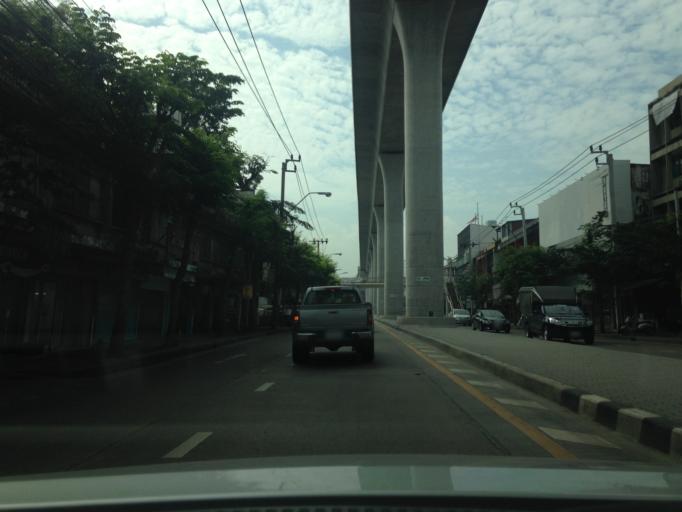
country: TH
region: Bangkok
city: Bang Sue
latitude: 13.8114
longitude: 100.5315
